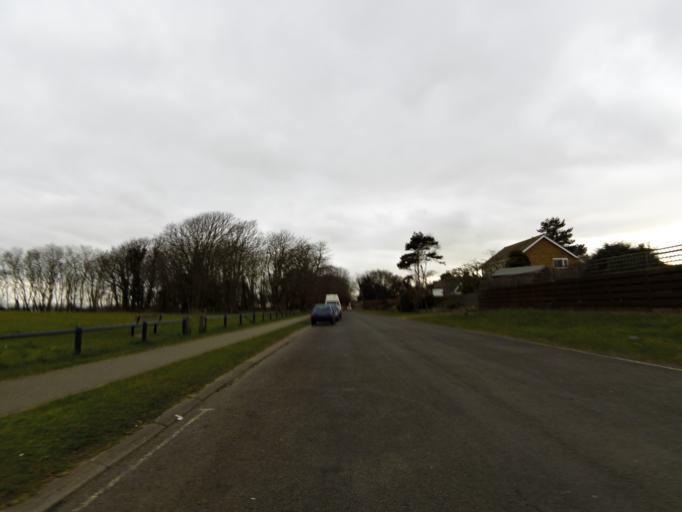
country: GB
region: England
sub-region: Suffolk
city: Felixstowe
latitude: 51.9692
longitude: 1.3725
